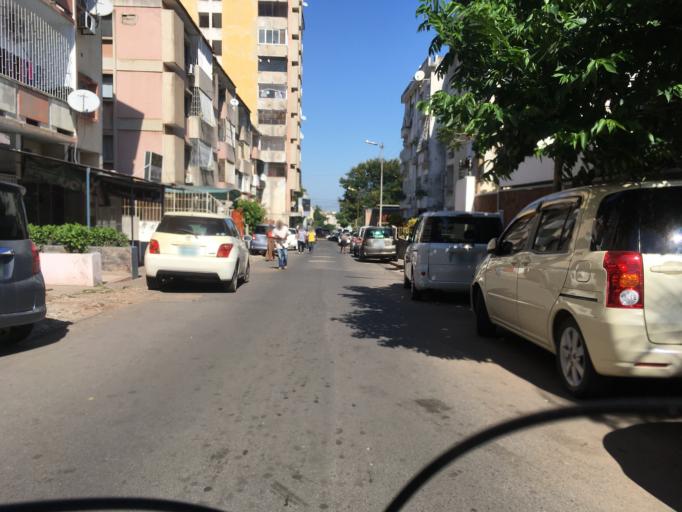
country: MZ
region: Maputo City
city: Maputo
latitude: -25.9684
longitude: 32.5800
